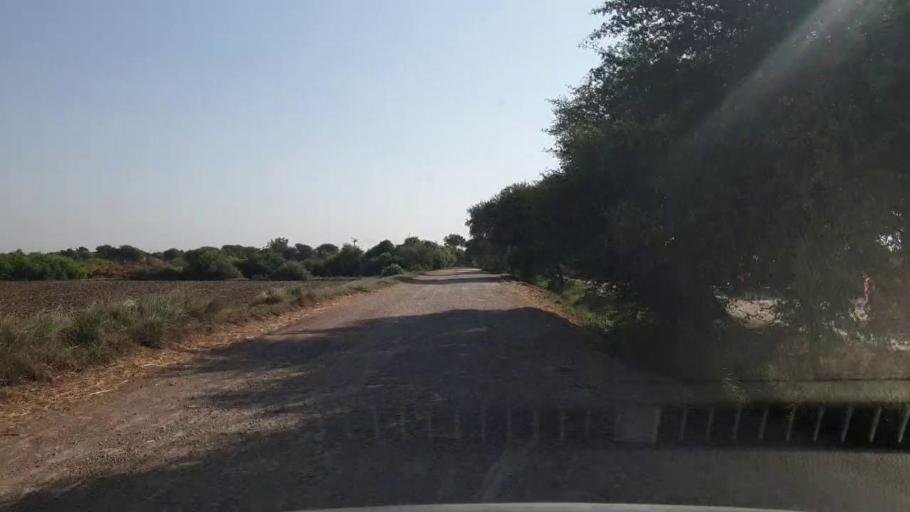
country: PK
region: Sindh
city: Matli
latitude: 25.0303
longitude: 68.7321
